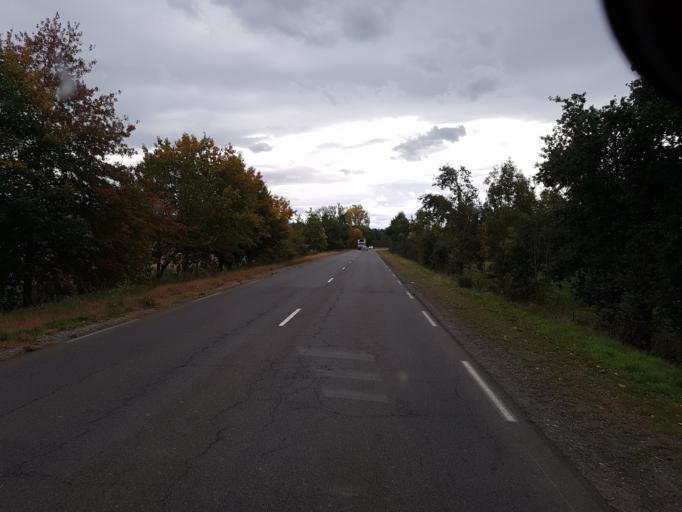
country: FR
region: Rhone-Alpes
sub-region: Departement de la Loire
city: Chamboeuf
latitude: 45.5692
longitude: 4.3076
